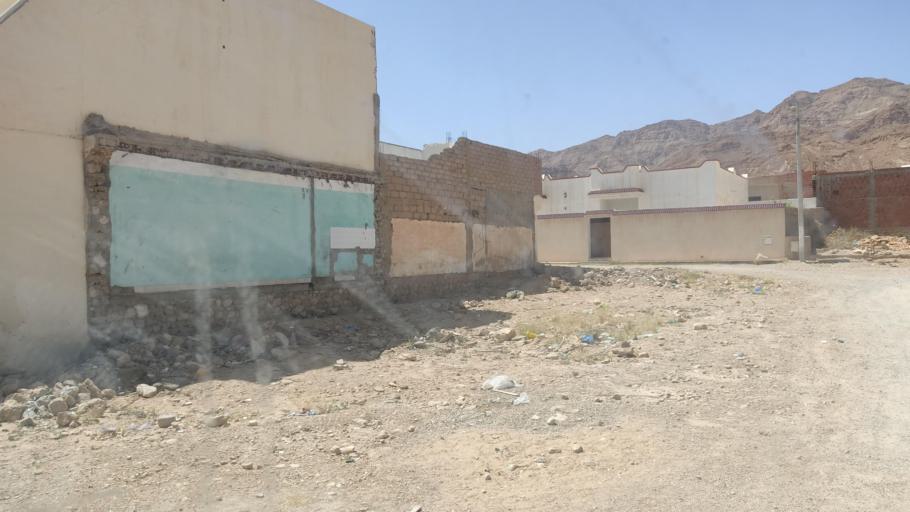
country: TN
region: Gafsa
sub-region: Gafsa Municipality
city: Gafsa
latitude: 34.3414
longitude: 8.9387
